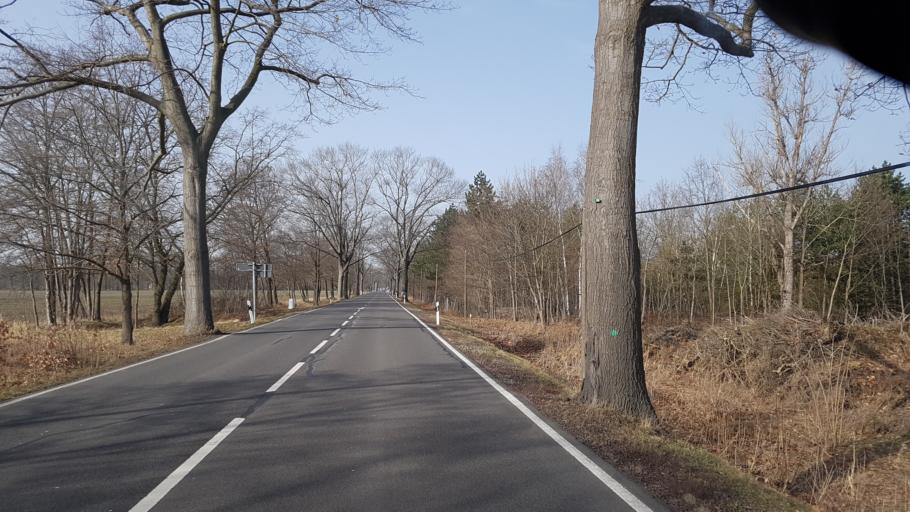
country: DE
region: Brandenburg
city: Cottbus
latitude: 51.7485
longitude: 14.3740
